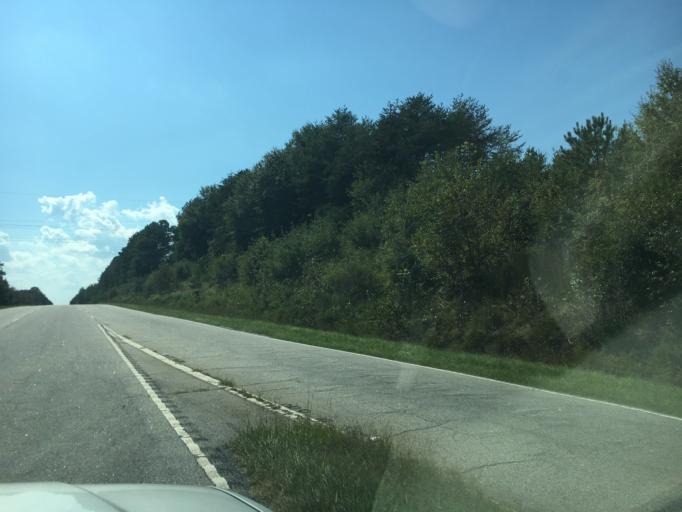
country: US
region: South Carolina
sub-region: Pickens County
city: Central
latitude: 34.7051
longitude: -82.7598
